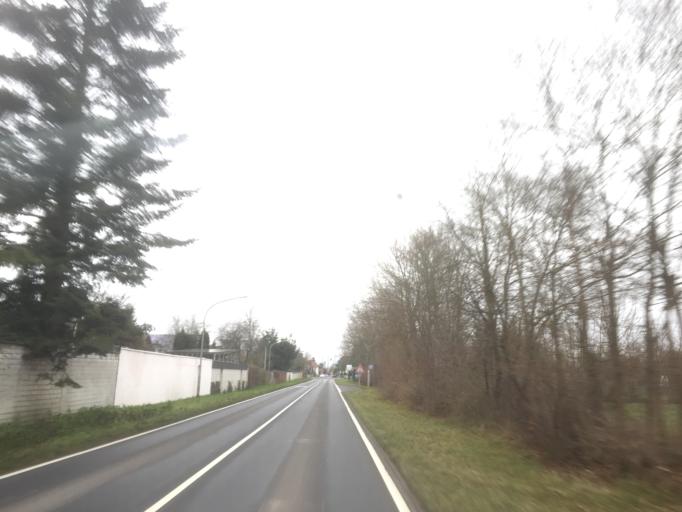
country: DE
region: Hesse
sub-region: Regierungsbezirk Darmstadt
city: Seligenstadt
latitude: 50.0344
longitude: 8.9843
